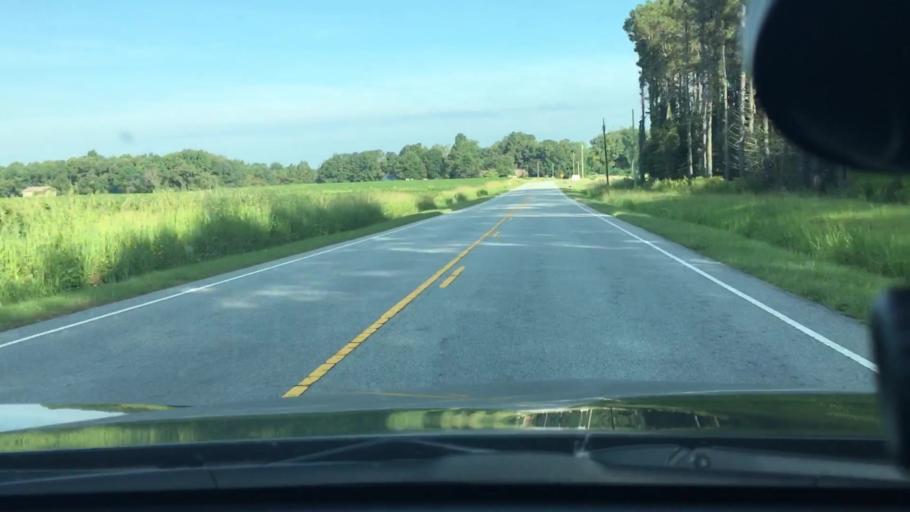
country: US
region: North Carolina
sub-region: Pitt County
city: Farmville
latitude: 35.7153
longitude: -77.5247
